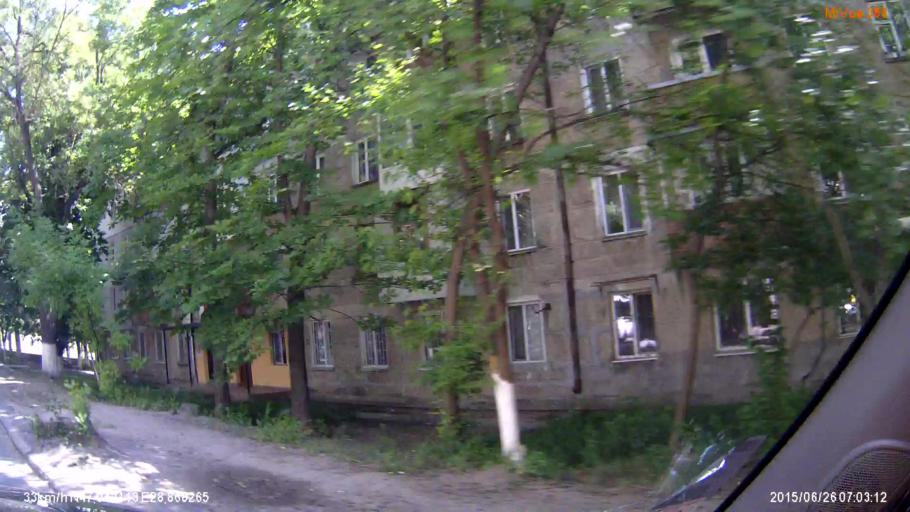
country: MD
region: Chisinau
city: Chisinau
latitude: 47.0420
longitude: 28.8682
